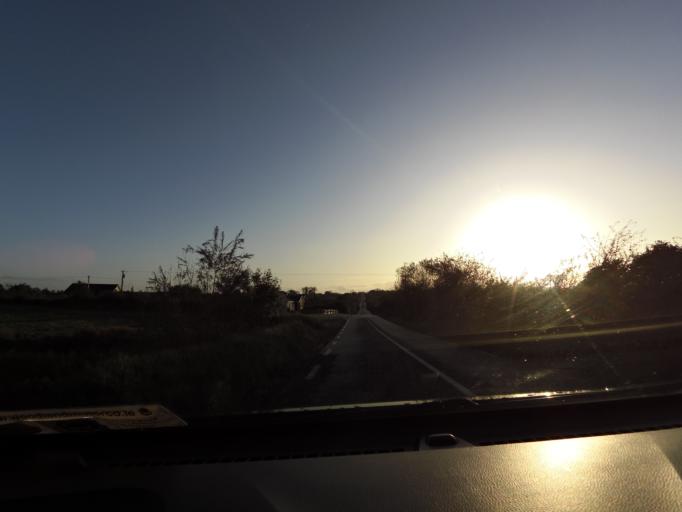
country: IE
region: Connaught
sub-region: Roscommon
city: Castlerea
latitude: 53.7497
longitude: -8.5313
